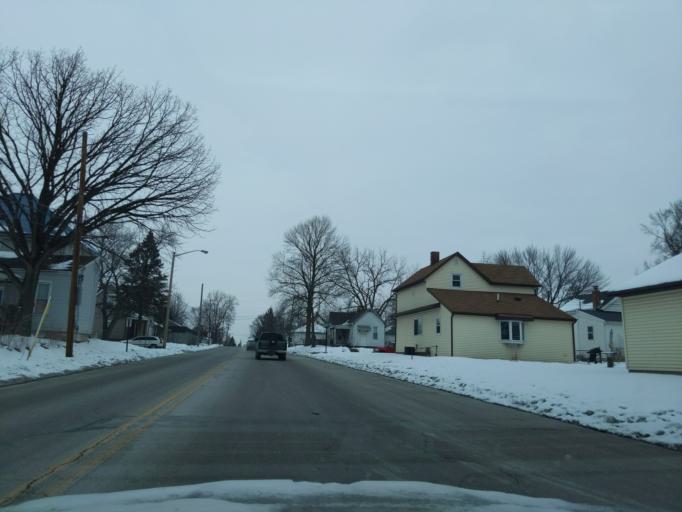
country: US
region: Indiana
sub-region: Tippecanoe County
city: Lafayette
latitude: 40.4118
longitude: -86.8771
